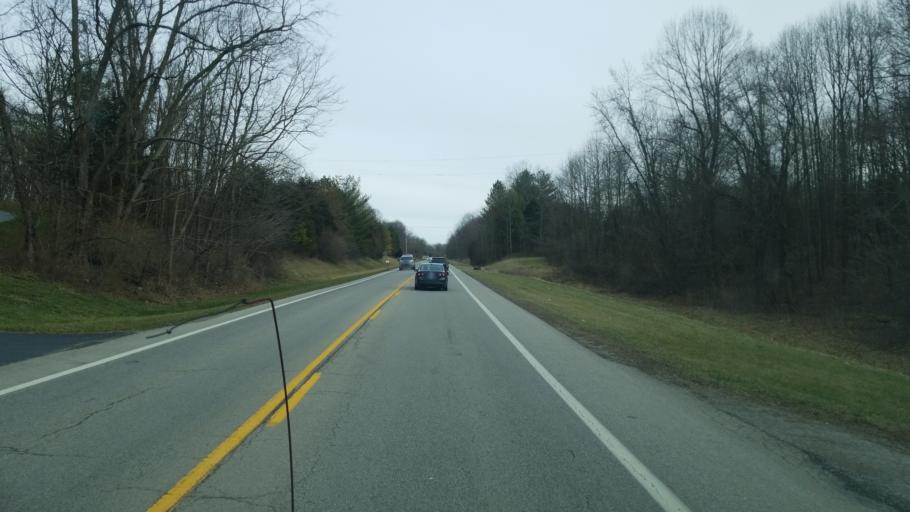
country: US
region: Ohio
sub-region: Highland County
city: Hillsboro
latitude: 39.1620
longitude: -83.6469
